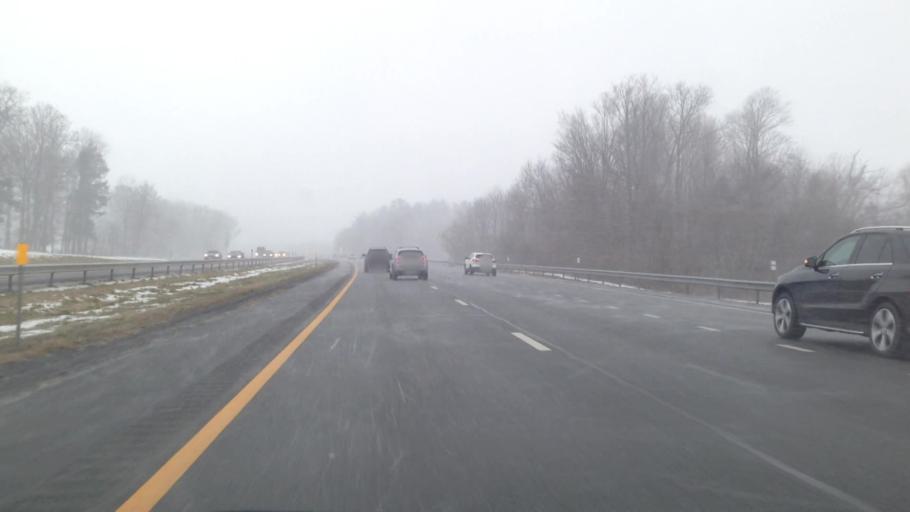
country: US
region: New York
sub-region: Montgomery County
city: Hagaman
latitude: 42.8976
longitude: -74.1009
